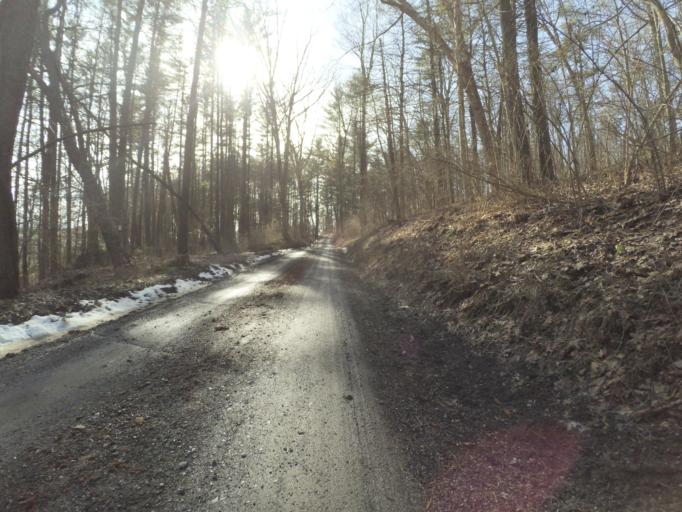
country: US
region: Pennsylvania
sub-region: Centre County
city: State College
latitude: 40.8265
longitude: -77.8623
